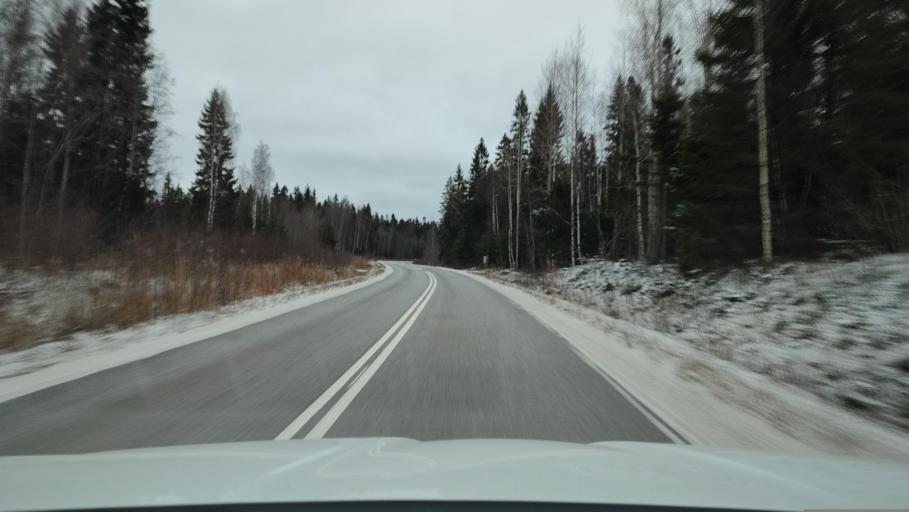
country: FI
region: Ostrobothnia
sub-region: Vaasa
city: Replot
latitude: 63.2927
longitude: 21.3548
